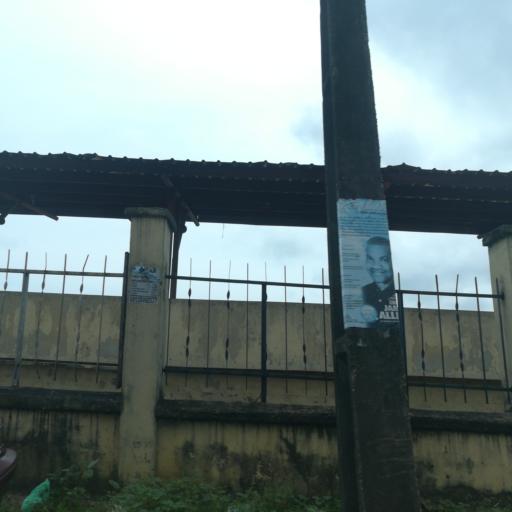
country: NG
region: Rivers
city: Port Harcourt
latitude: 4.8025
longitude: 7.0046
